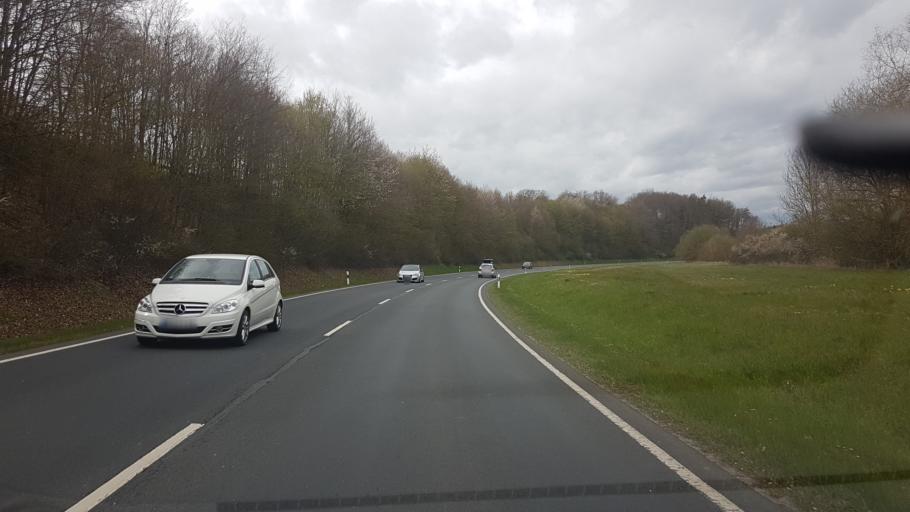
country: DE
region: Bavaria
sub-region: Regierungsbezirk Unterfranken
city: Wuelfershausen
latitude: 50.3281
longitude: 10.3248
